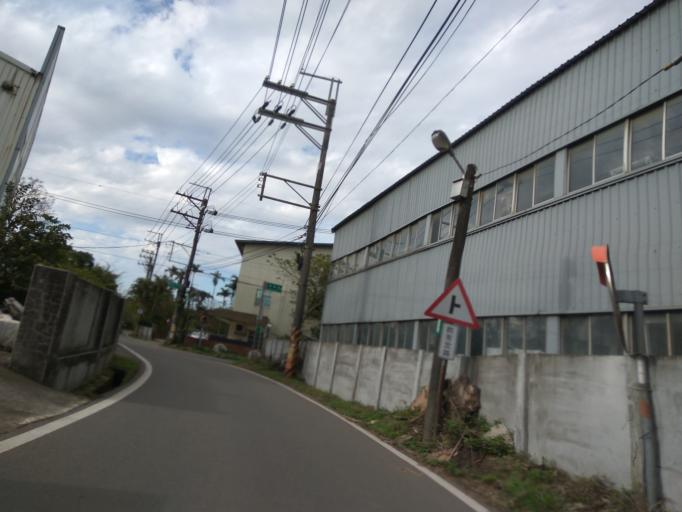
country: TW
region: Taiwan
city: Daxi
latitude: 24.9398
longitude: 121.1737
